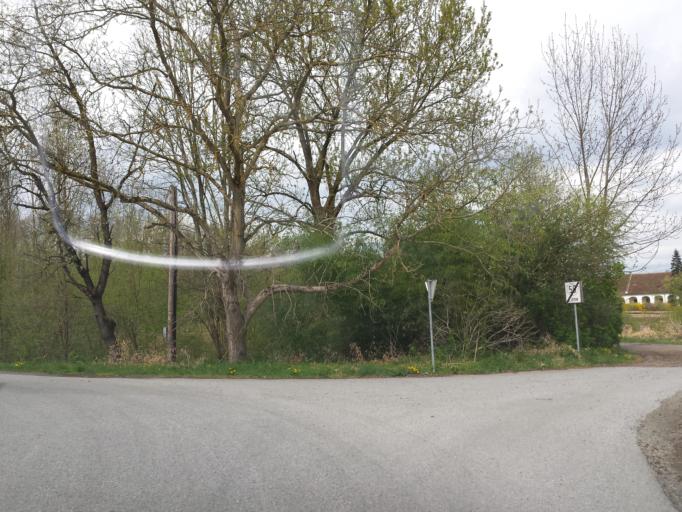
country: AT
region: Styria
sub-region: Politischer Bezirk Hartberg-Fuerstenfeld
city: Loipersdorf bei Fuerstenfeld
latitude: 47.0120
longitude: 16.1305
